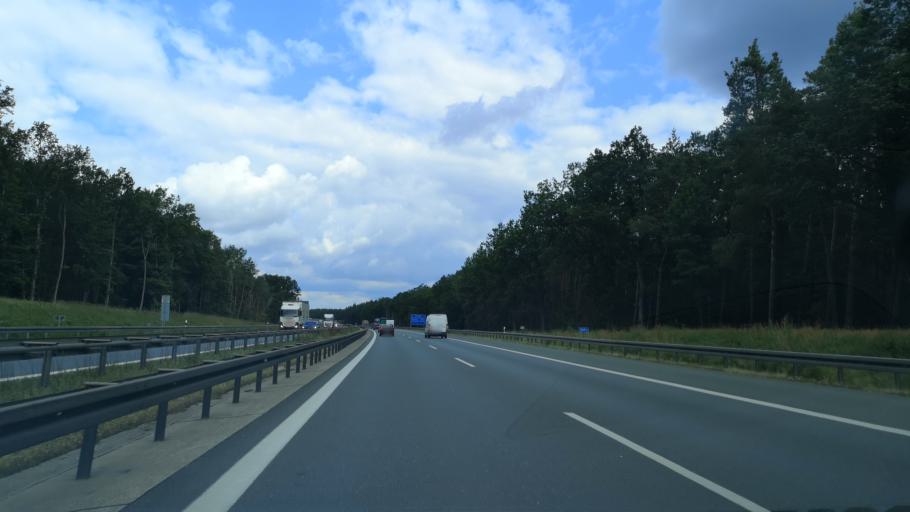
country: DE
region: Bavaria
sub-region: Regierungsbezirk Mittelfranken
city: Hessdorf
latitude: 49.6341
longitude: 10.9165
